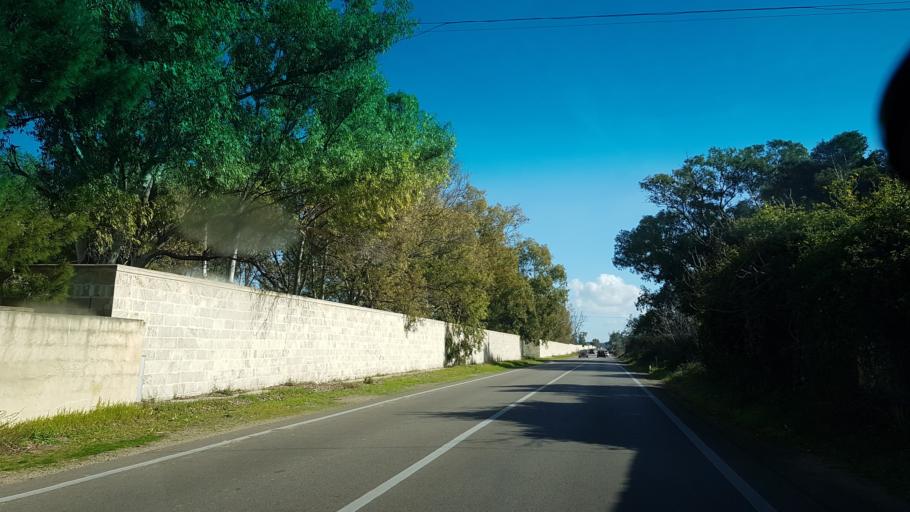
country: IT
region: Apulia
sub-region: Provincia di Lecce
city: Arnesano
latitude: 40.3591
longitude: 18.1119
